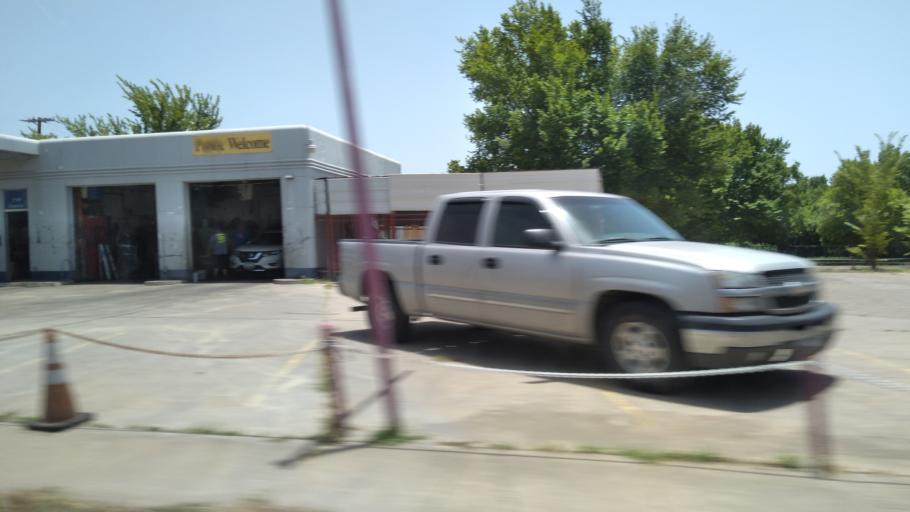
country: US
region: Texas
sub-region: McLennan County
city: Waco
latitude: 31.5369
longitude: -97.1524
